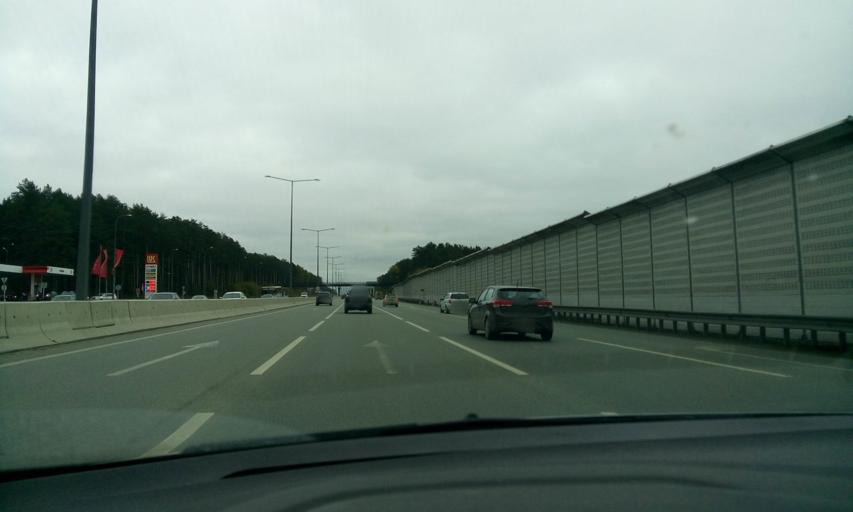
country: RU
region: Sverdlovsk
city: Yekaterinburg
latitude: 56.7891
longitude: 60.6746
